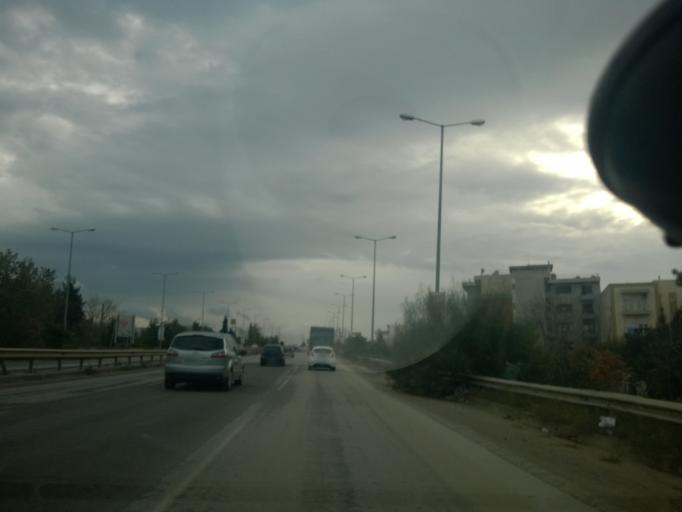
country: GR
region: Central Macedonia
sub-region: Nomos Thessalonikis
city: Kalamaria
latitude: 40.5889
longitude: 22.9686
